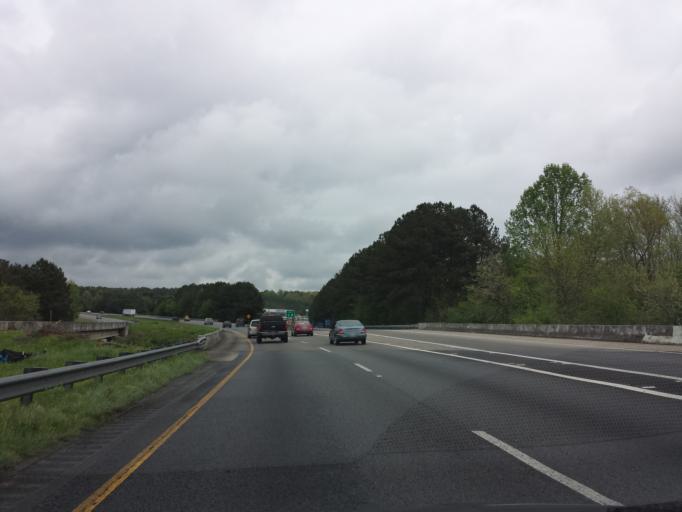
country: US
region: Georgia
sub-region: Cherokee County
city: Woodstock
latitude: 34.0991
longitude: -84.5303
